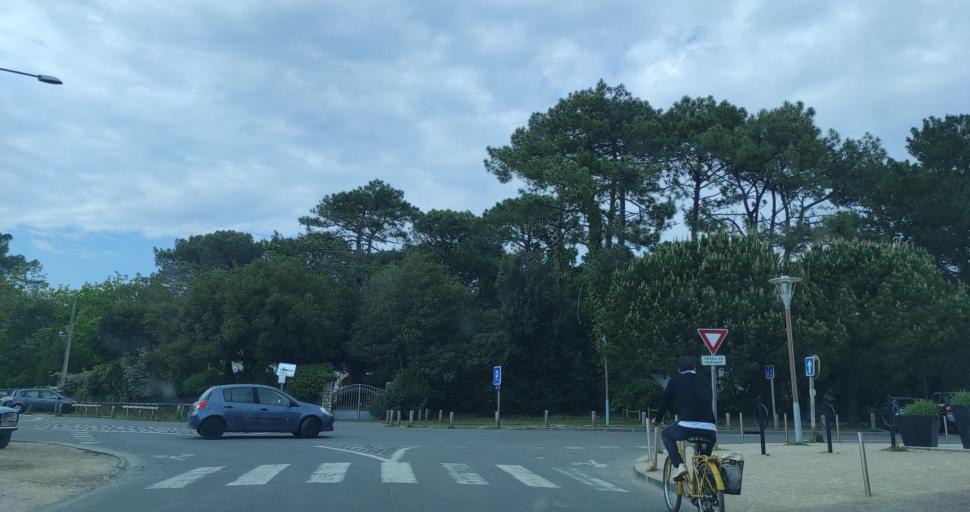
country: FR
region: Aquitaine
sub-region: Departement de la Gironde
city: Arcachon
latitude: 44.6563
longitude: -1.2418
